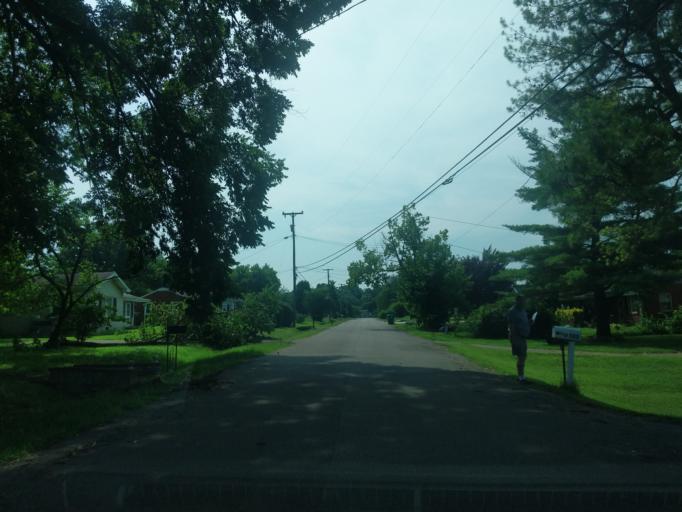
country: US
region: Tennessee
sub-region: Davidson County
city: Lakewood
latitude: 36.2739
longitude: -86.6692
